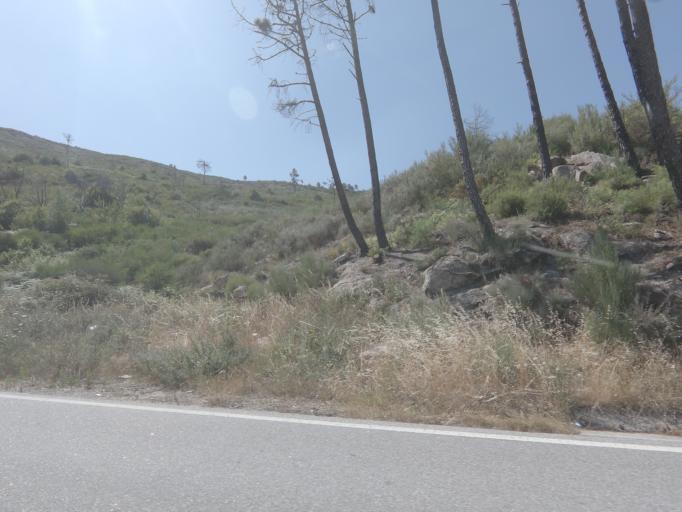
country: PT
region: Viseu
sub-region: Tarouca
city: Tarouca
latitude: 40.9995
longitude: -7.7815
